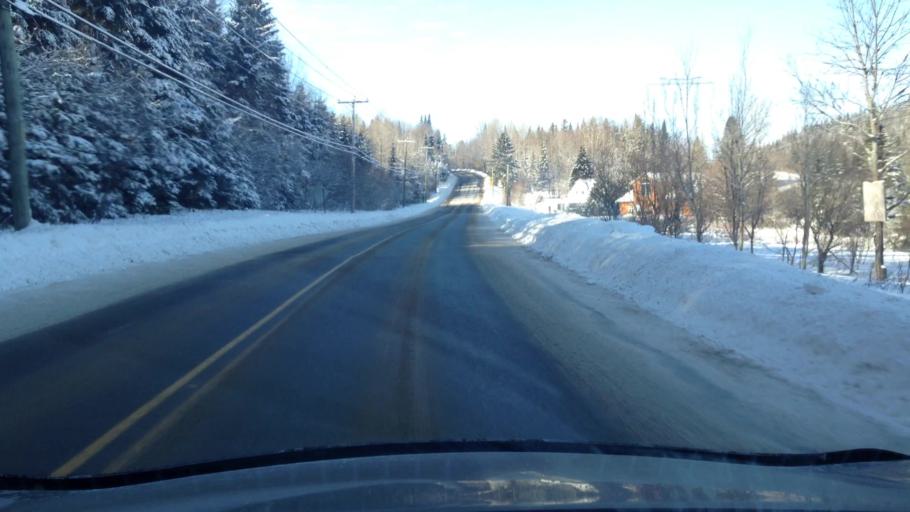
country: CA
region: Quebec
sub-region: Laurentides
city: Sainte-Agathe-des-Monts
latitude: 45.9324
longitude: -74.4327
